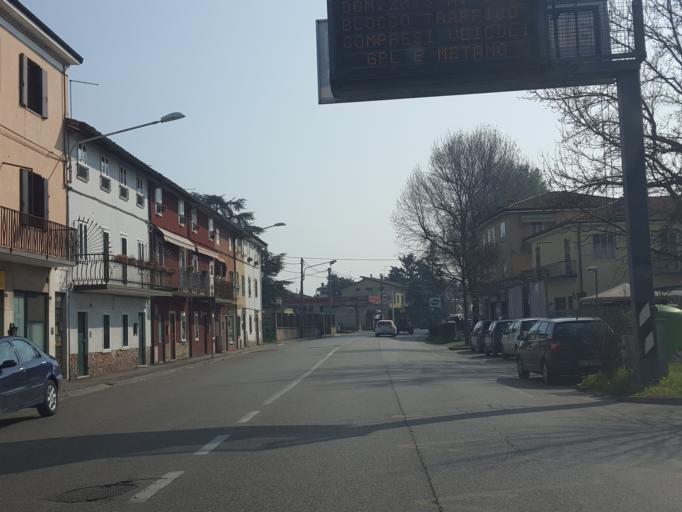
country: IT
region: Veneto
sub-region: Provincia di Vicenza
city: Vicenza
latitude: 45.5574
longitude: 11.5257
